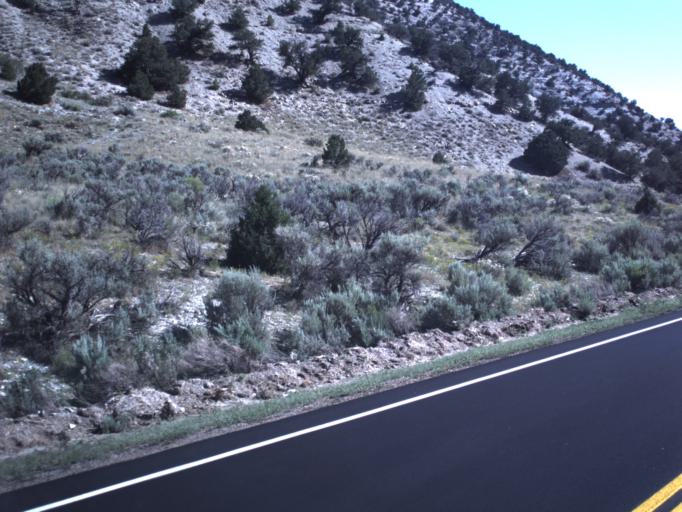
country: US
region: Utah
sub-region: Duchesne County
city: Duchesne
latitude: 39.9614
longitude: -110.6413
